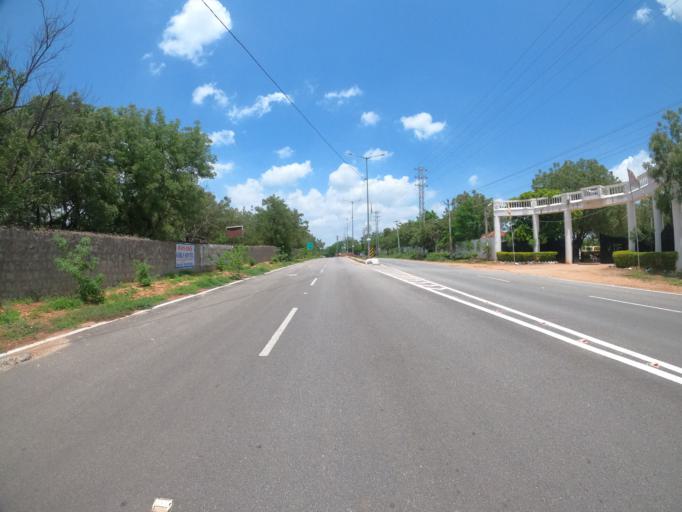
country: IN
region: Telangana
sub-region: Rangareddi
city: Sriramnagar
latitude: 17.3544
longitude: 78.3295
